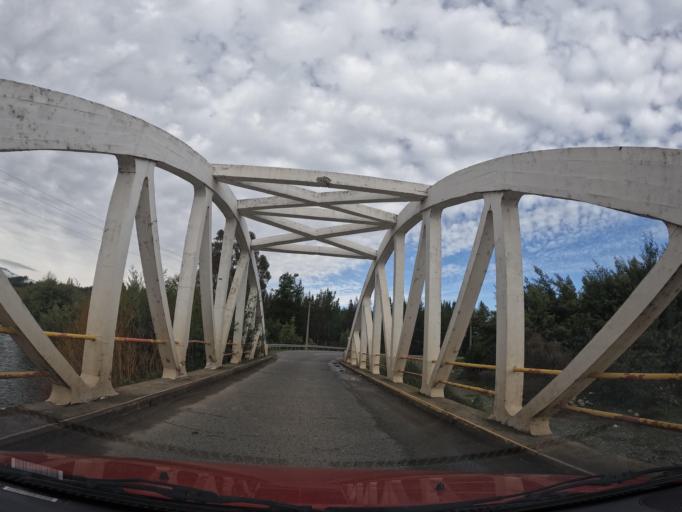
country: CL
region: Maule
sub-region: Provincia de Linares
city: Linares
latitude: -35.9088
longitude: -71.4912
